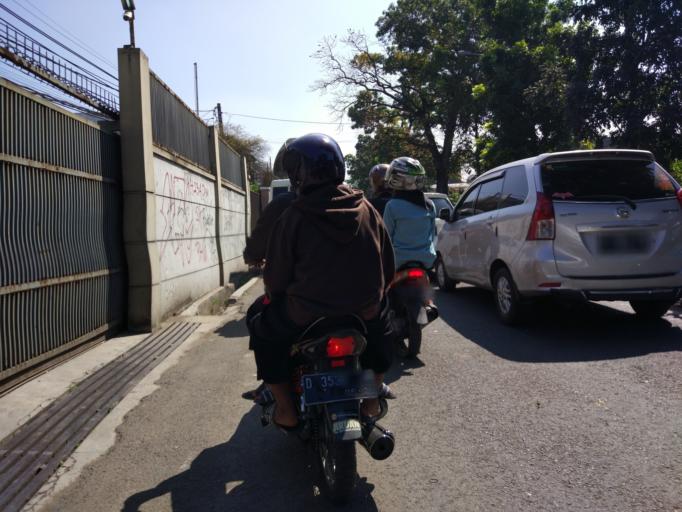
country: ID
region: West Java
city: Bandung
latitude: -6.9328
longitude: 107.6065
